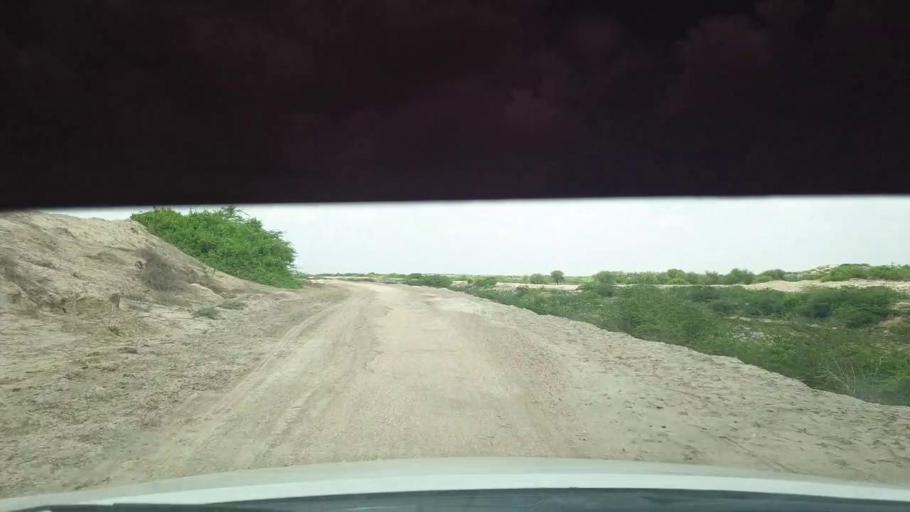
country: PK
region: Sindh
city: Kadhan
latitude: 24.5067
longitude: 69.1179
